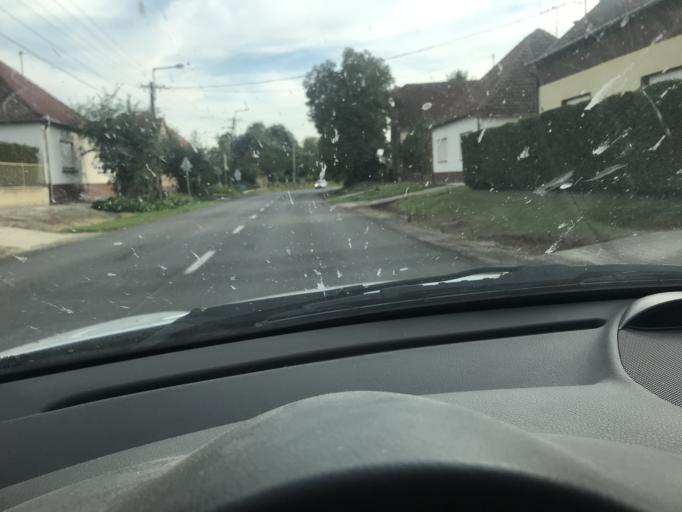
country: HU
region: Bacs-Kiskun
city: Csaszartoltes
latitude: 46.4277
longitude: 19.1815
